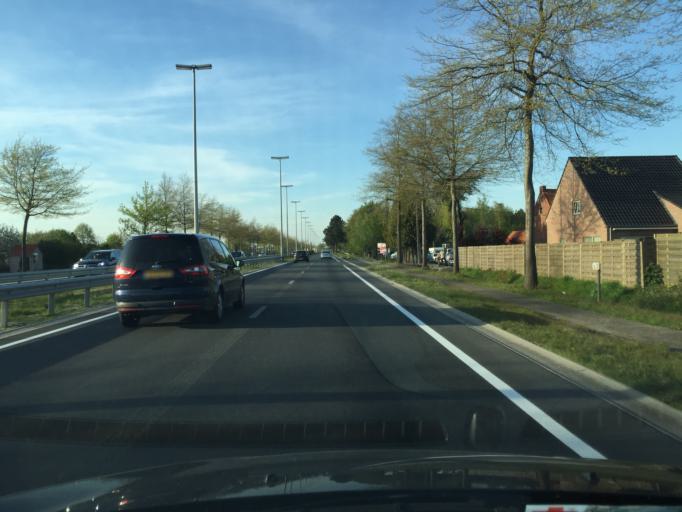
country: BE
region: Flanders
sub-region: Provincie Oost-Vlaanderen
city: Maldegem
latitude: 51.1865
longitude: 3.4511
